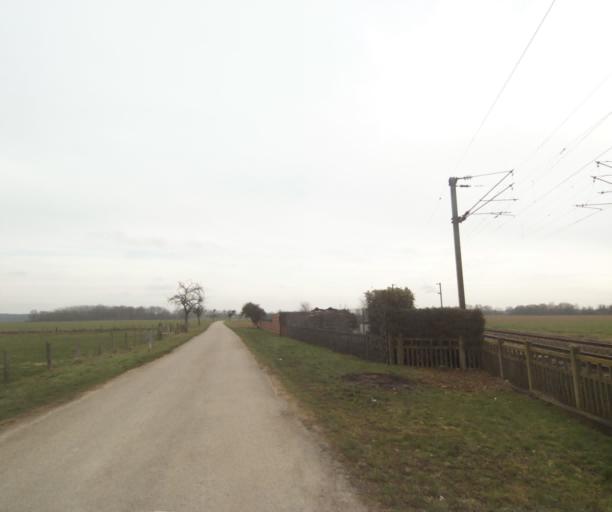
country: FR
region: Champagne-Ardenne
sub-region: Departement de la Haute-Marne
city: Villiers-en-Lieu
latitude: 48.6733
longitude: 4.8782
